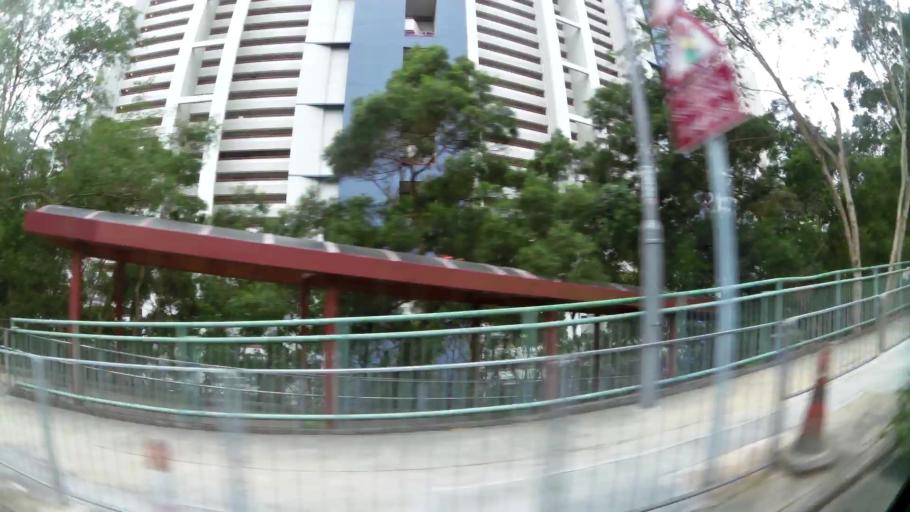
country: HK
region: Tsuen Wan
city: Tsuen Wan
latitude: 22.3801
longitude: 114.1368
